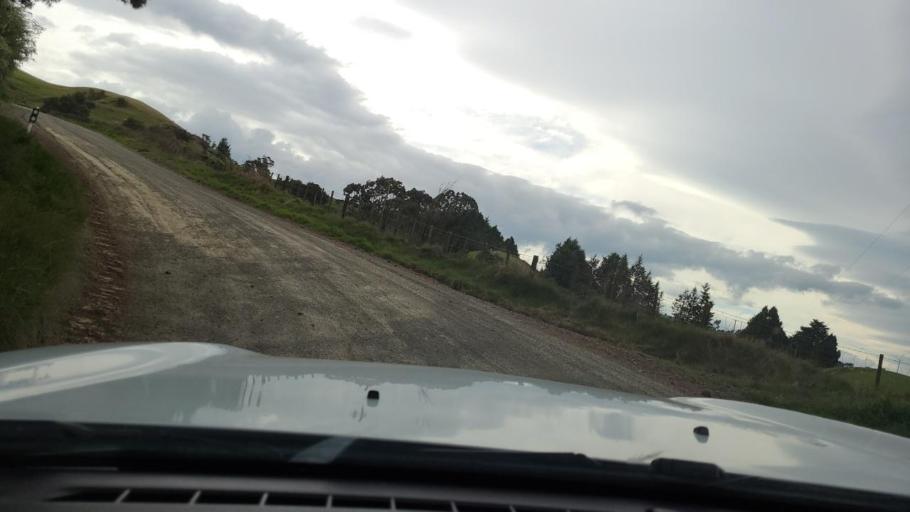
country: NZ
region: Hawke's Bay
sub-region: Napier City
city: Napier
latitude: -39.2998
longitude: 176.8340
